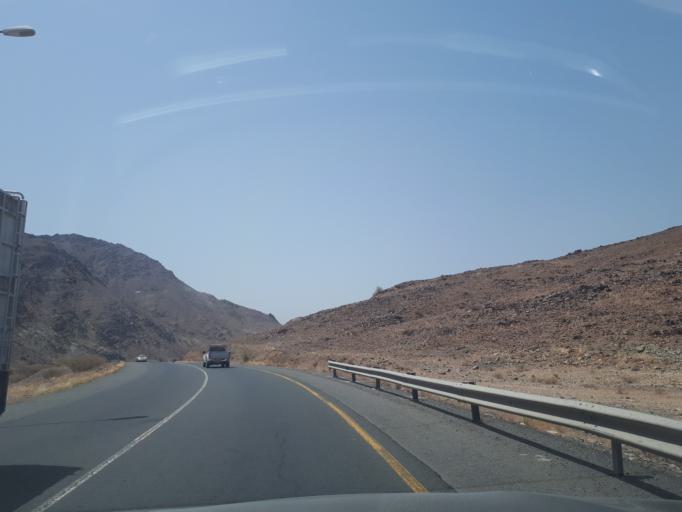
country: OM
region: Muhafazat ad Dakhiliyah
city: Sufalat Sama'il
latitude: 23.2414
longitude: 58.0821
